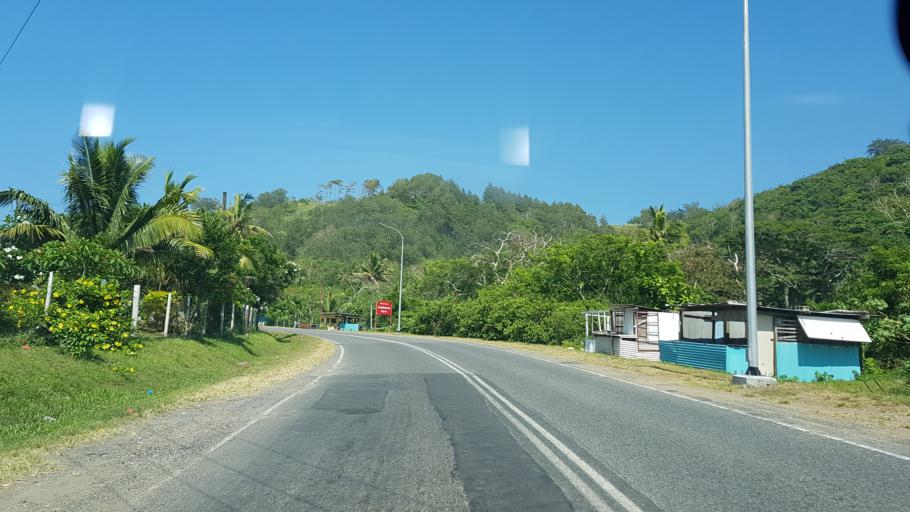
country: FJ
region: Western
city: Nadi
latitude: -18.1815
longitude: 177.6070
